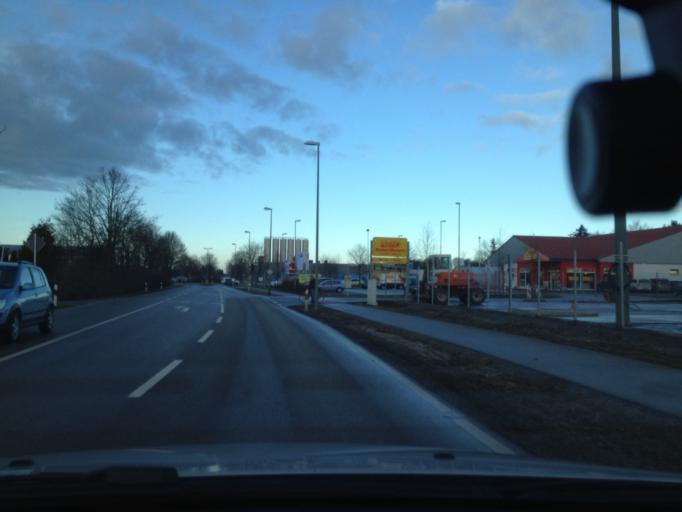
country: DE
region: Bavaria
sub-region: Swabia
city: Schwabmunchen
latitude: 48.1644
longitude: 10.7569
